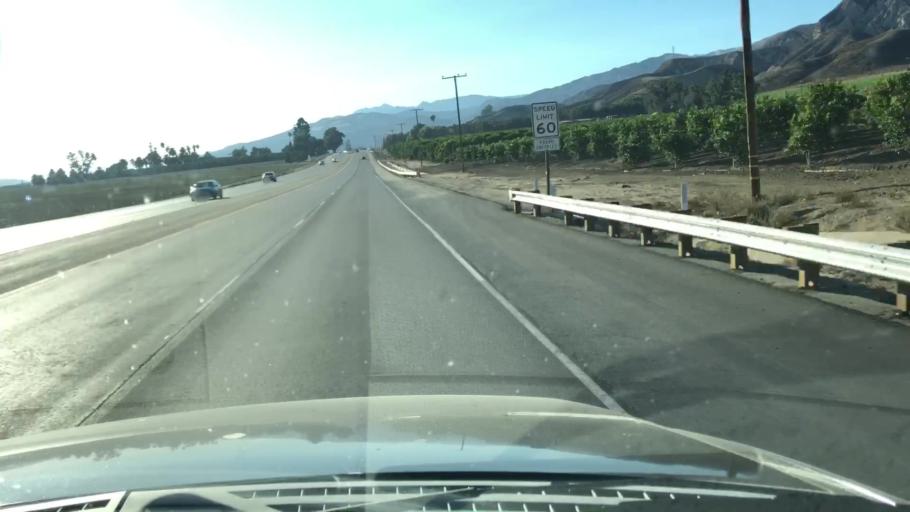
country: US
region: California
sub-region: Ventura County
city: Piru
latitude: 34.4056
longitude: -118.7465
